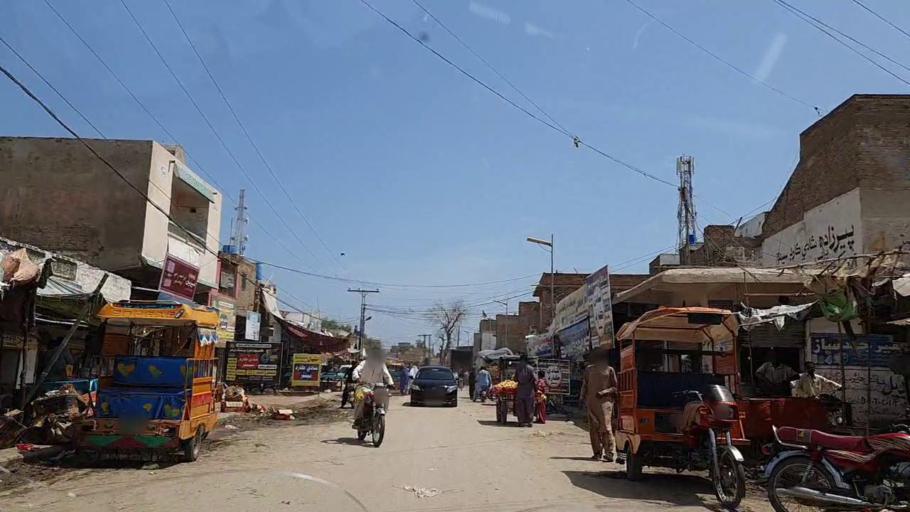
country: PK
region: Sindh
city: Naushahro Firoz
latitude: 26.8411
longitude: 68.1191
